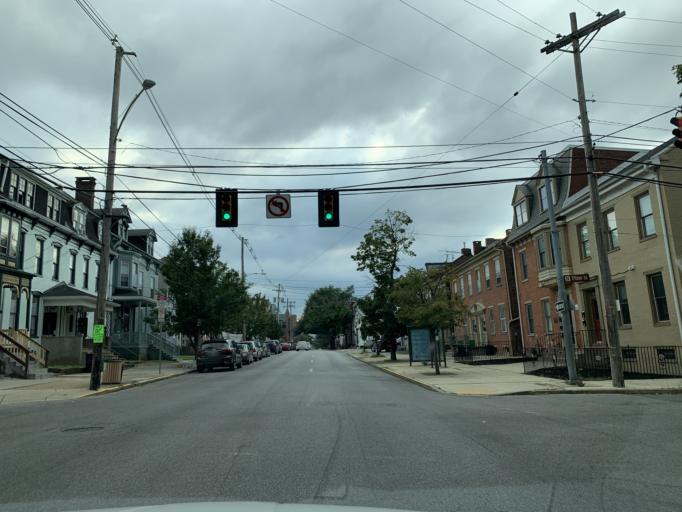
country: US
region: Pennsylvania
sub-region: York County
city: York
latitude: 39.9658
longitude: -76.7224
